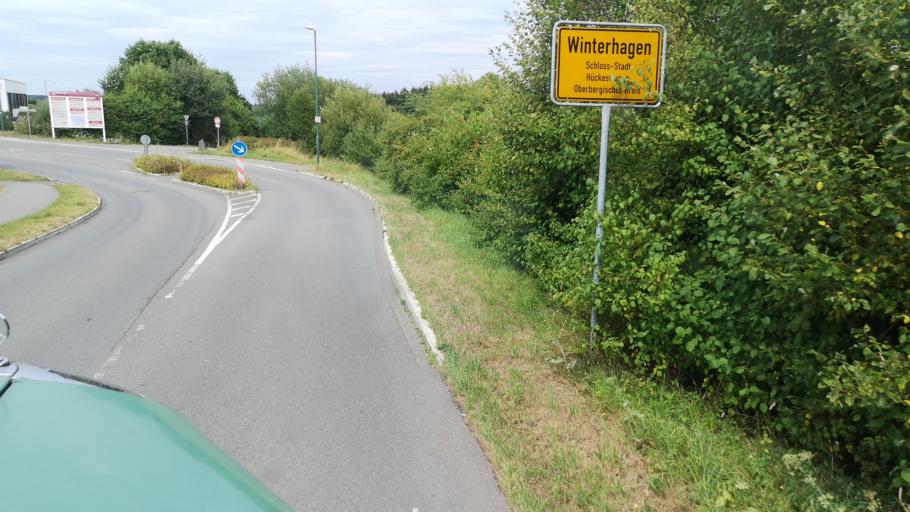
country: DE
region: North Rhine-Westphalia
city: Huckeswagen
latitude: 51.1392
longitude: 7.2988
